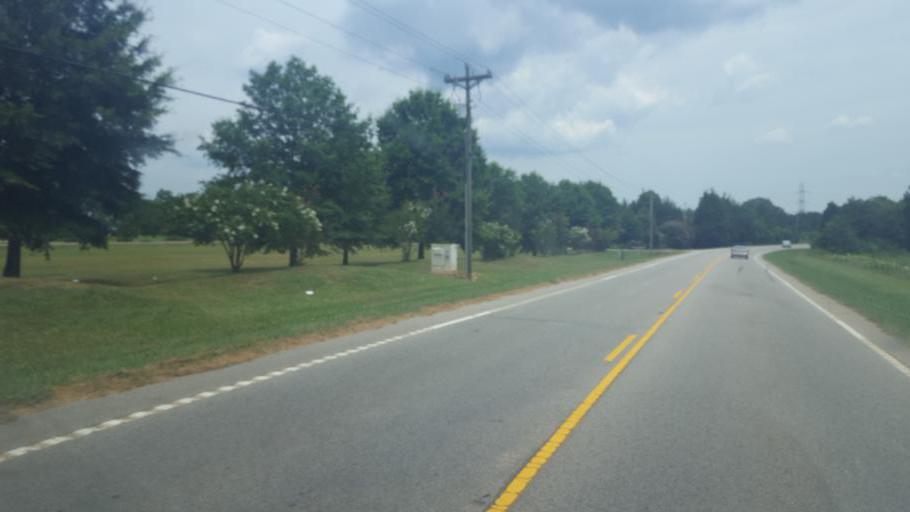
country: US
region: South Carolina
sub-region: York County
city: Newport
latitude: 34.9627
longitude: -81.1417
